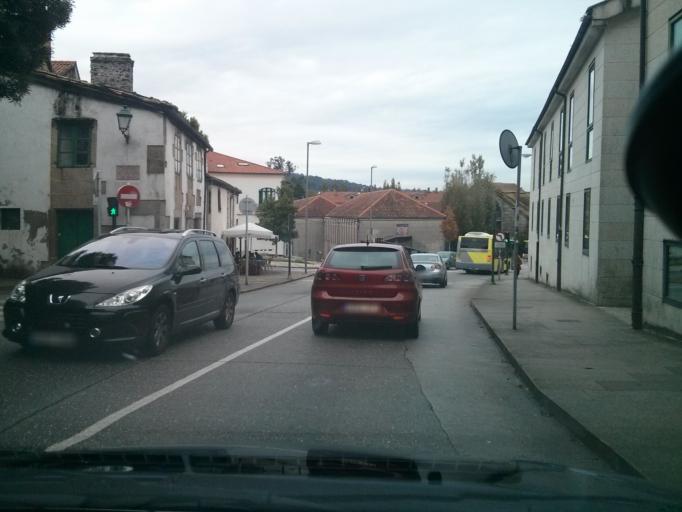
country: ES
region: Galicia
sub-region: Provincia da Coruna
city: Santiago de Compostela
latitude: 42.8801
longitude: -8.5494
